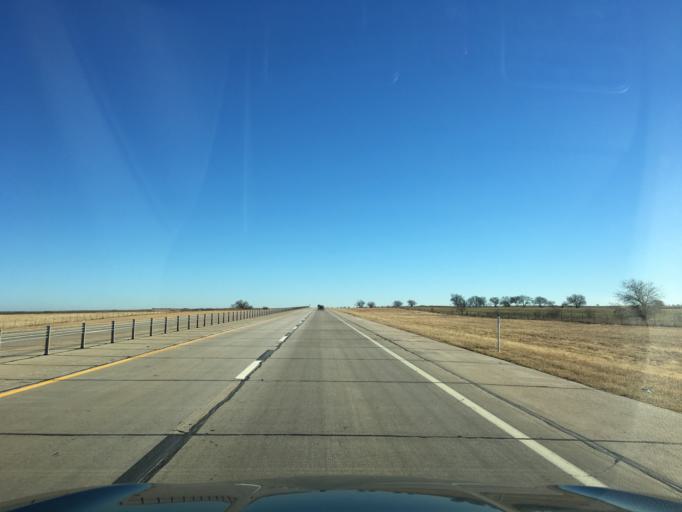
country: US
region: Oklahoma
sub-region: Noble County
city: Perry
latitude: 36.4008
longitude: -97.2452
